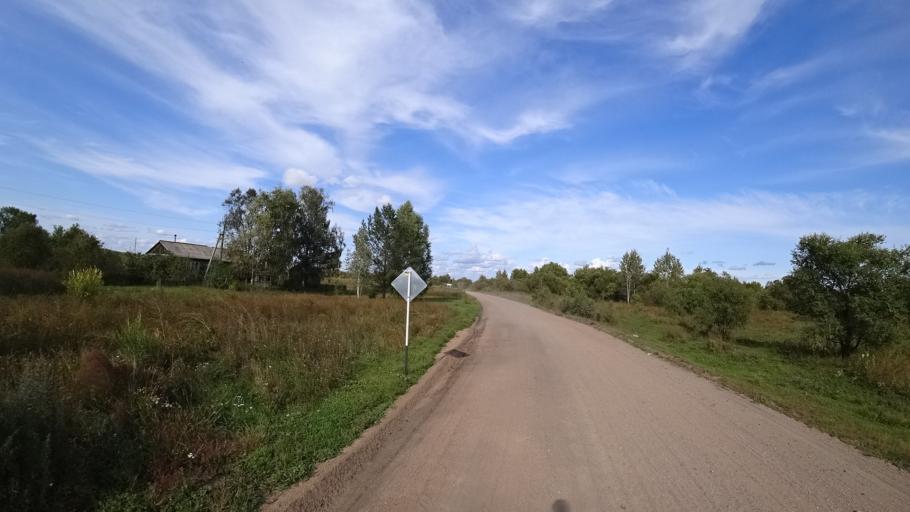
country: RU
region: Amur
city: Arkhara
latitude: 49.3669
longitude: 130.1303
